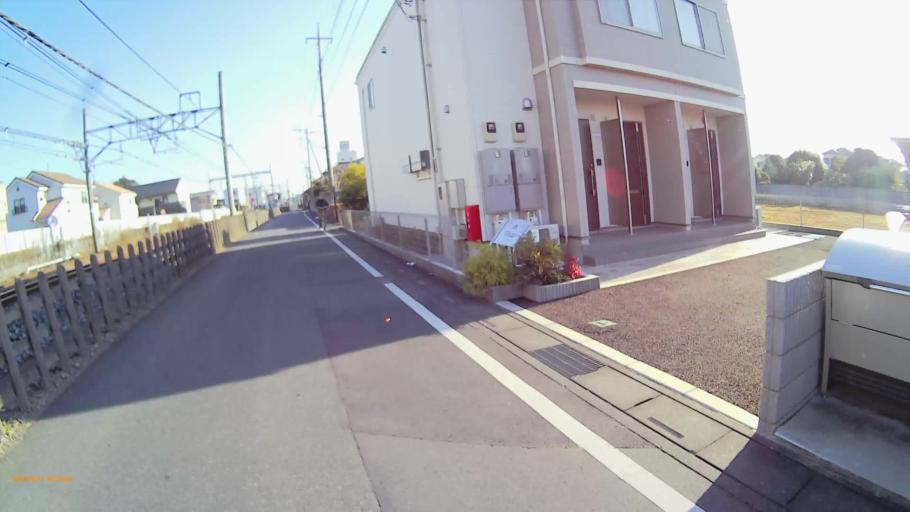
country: JP
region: Saitama
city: Konosu
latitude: 36.0368
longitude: 139.5303
